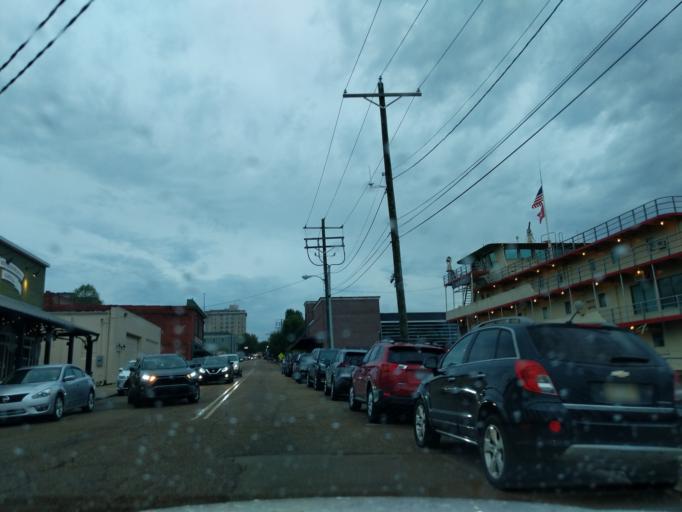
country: US
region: Mississippi
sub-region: Warren County
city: Vicksburg
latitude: 32.3542
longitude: -90.8815
